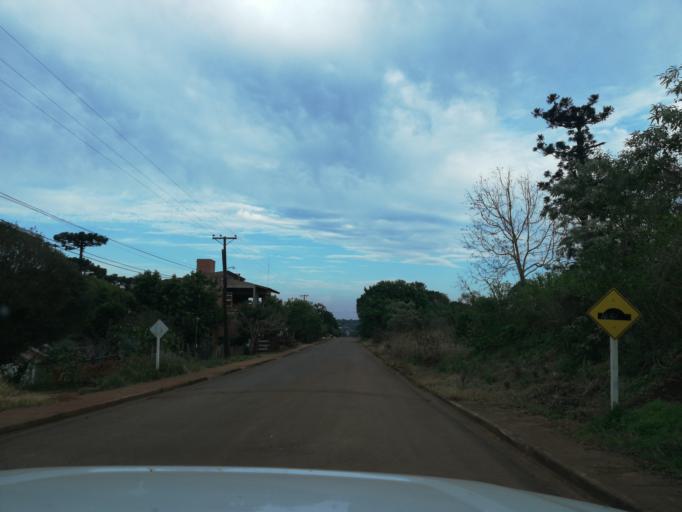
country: AR
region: Misiones
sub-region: Departamento de San Pedro
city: San Pedro
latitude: -26.6258
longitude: -54.1011
